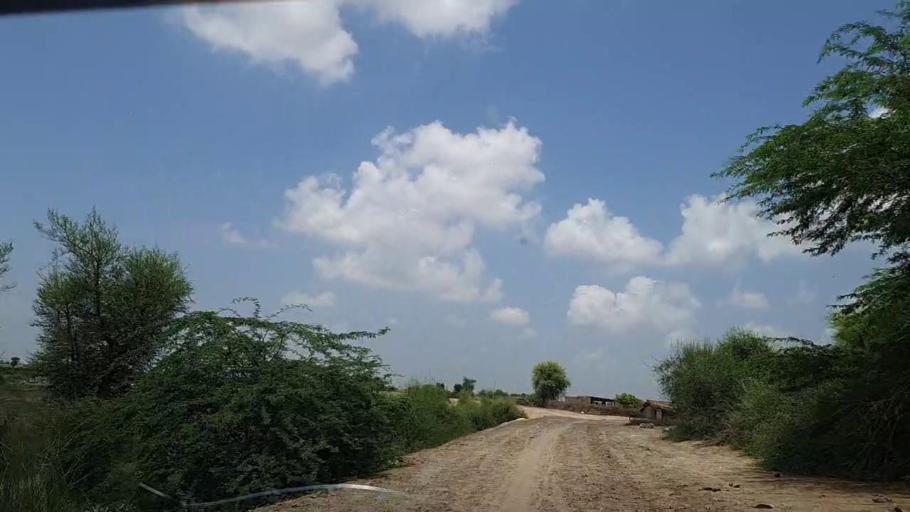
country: PK
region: Sindh
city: Tharu Shah
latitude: 26.9642
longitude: 68.0307
